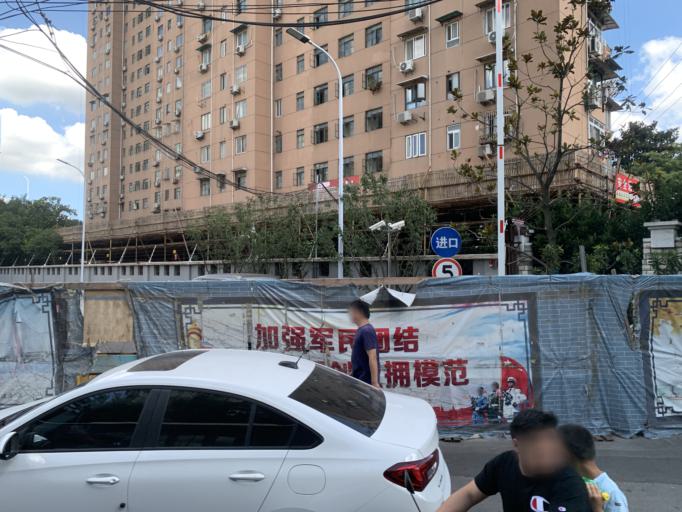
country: CN
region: Shanghai Shi
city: Pudong
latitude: 31.2480
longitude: 121.5533
